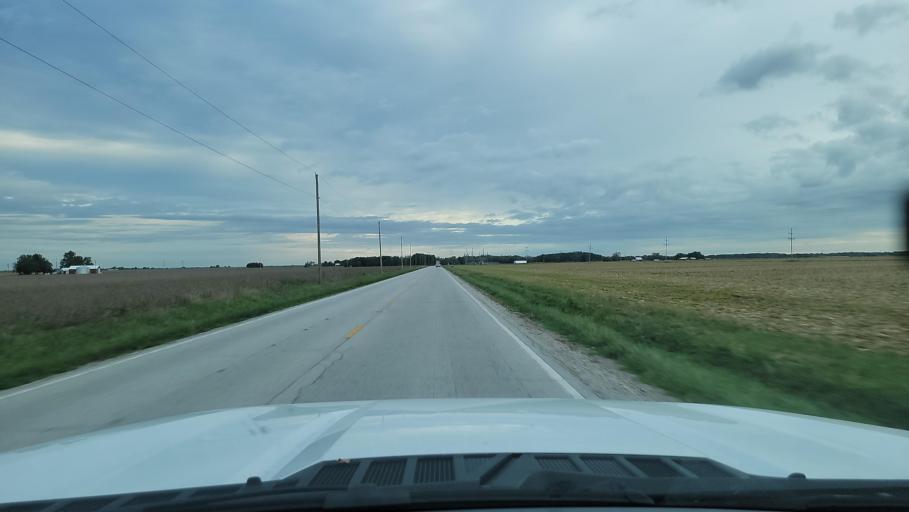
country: US
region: Illinois
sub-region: Schuyler County
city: Rushville
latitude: 40.1410
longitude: -90.5597
